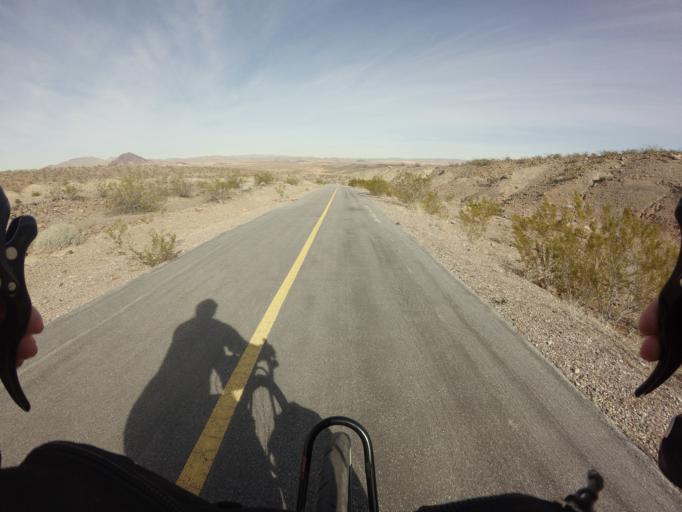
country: US
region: Nevada
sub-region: Clark County
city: Henderson
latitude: 36.1082
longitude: -114.8857
